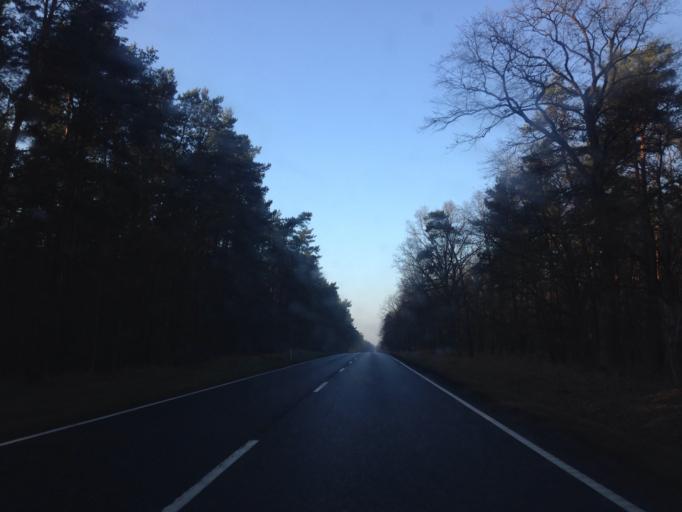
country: PL
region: Kujawsko-Pomorskie
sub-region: Powiat torunski
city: Zlawies Wielka
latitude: 53.0305
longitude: 18.4108
